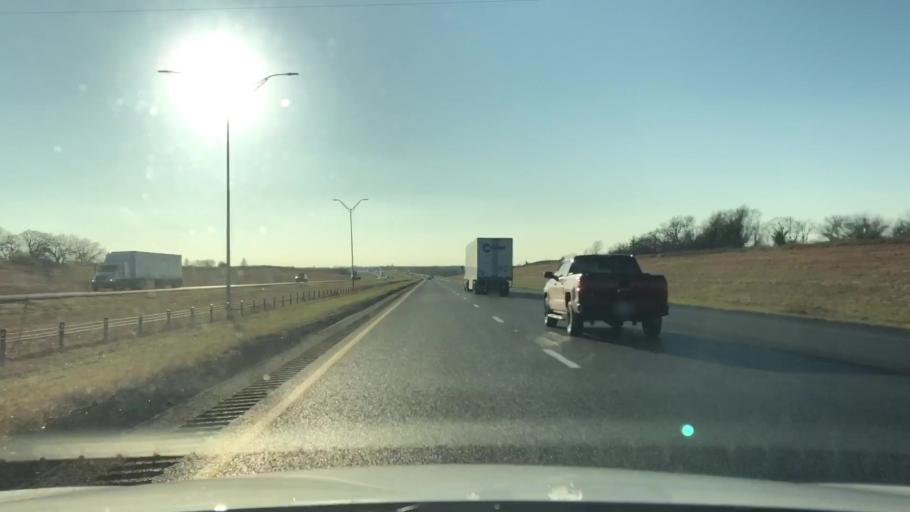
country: US
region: Texas
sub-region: Gonzales County
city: Waelder
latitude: 29.6874
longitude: -97.2573
